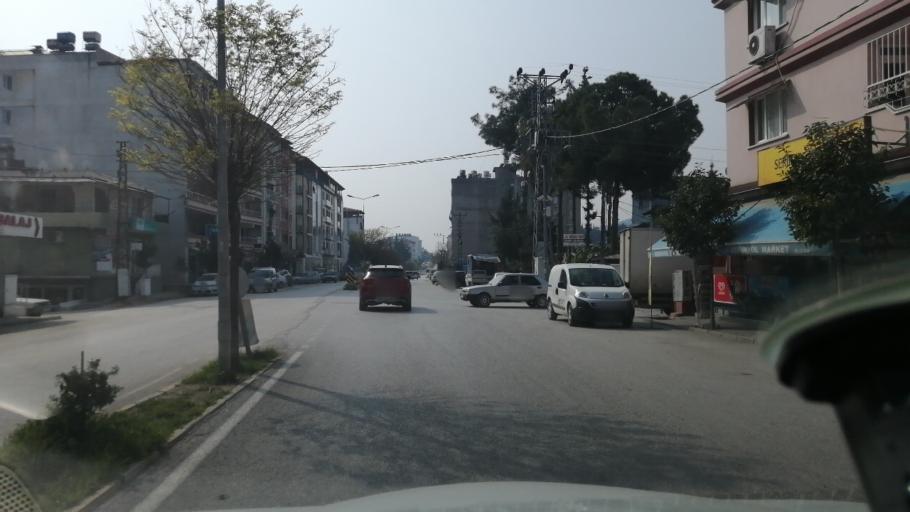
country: TR
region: Hatay
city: Serinyol
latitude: 36.3593
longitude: 36.2103
